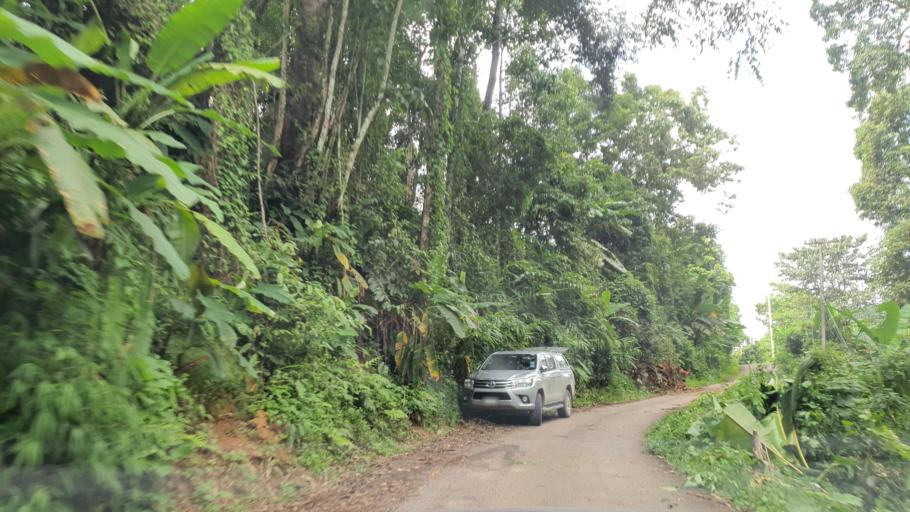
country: TH
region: Chiang Mai
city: Mae On
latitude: 18.9303
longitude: 99.3117
